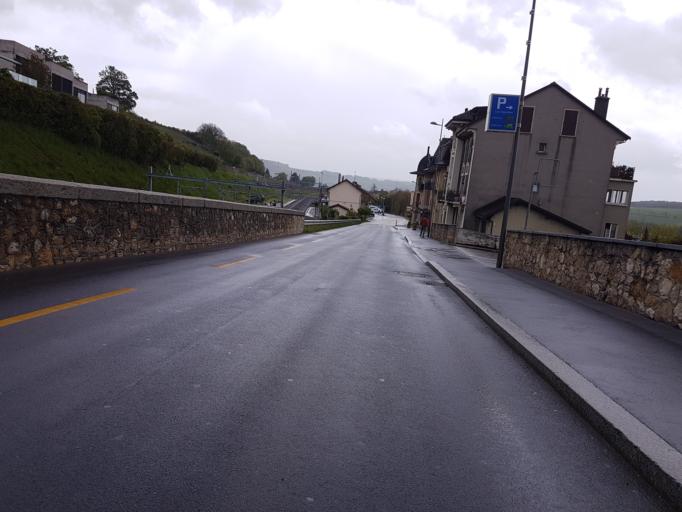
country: CH
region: Vaud
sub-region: Morges District
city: La Sarraz
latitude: 46.6597
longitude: 6.5159
